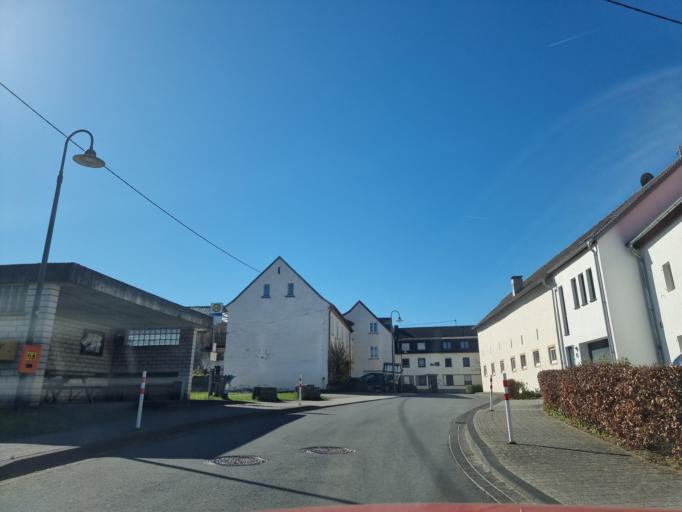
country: DE
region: Rheinland-Pfalz
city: Niederweis
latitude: 49.8715
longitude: 6.4659
